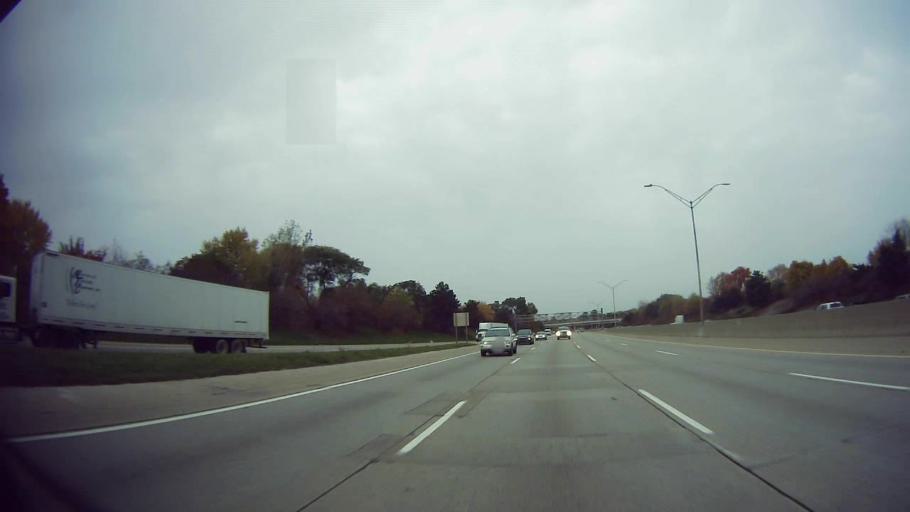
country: US
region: Michigan
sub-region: Macomb County
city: Center Line
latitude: 42.4888
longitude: -83.0520
